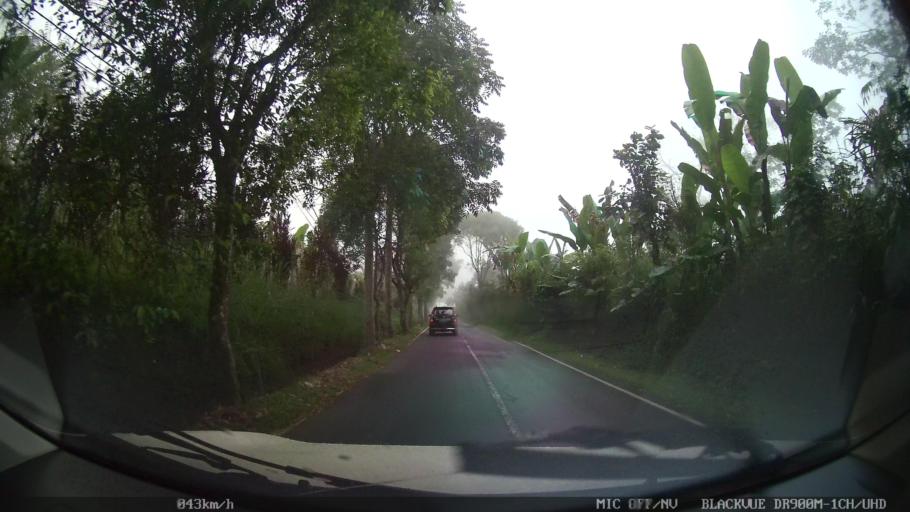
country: ID
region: Bali
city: Banjar Taro Kelod
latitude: -8.3282
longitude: 115.2911
